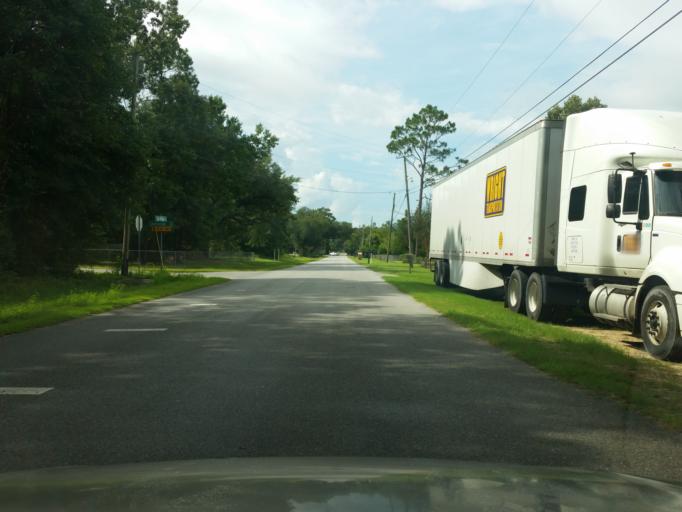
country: US
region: Florida
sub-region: Escambia County
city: Ensley
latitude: 30.5377
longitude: -87.3214
